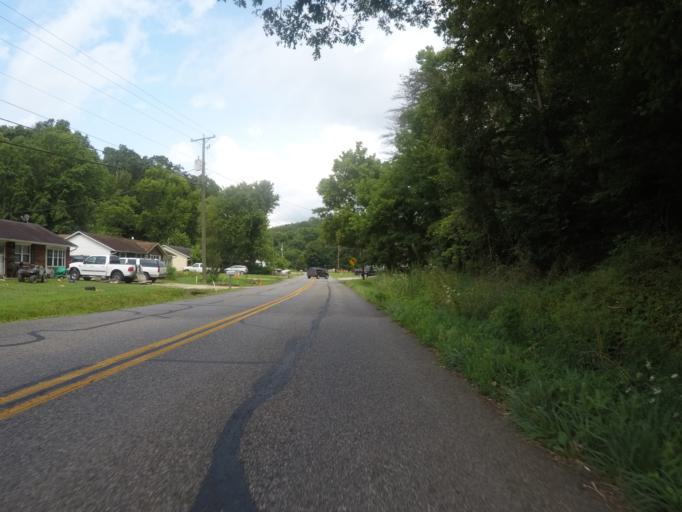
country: US
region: Kentucky
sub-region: Boyd County
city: Meads
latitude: 38.4146
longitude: -82.6826
